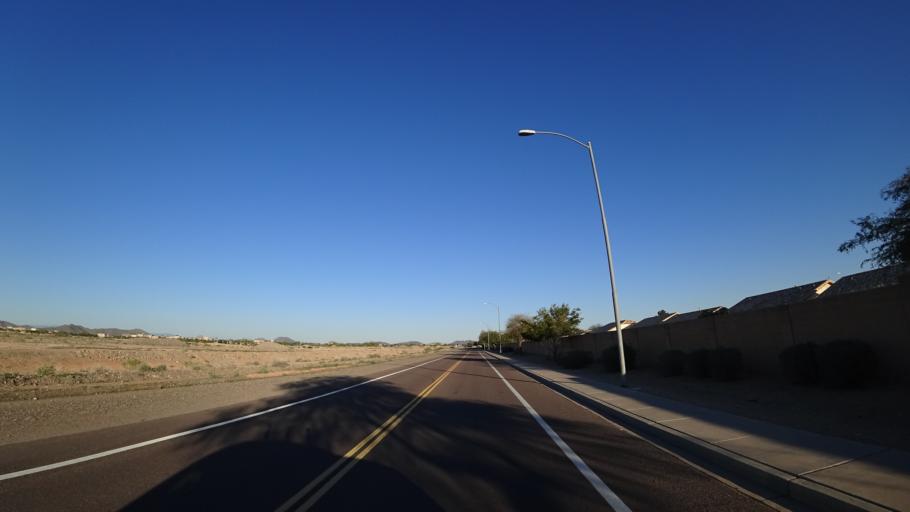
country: US
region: Arizona
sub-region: Maricopa County
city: Sun City West
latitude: 33.6744
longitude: -112.2837
